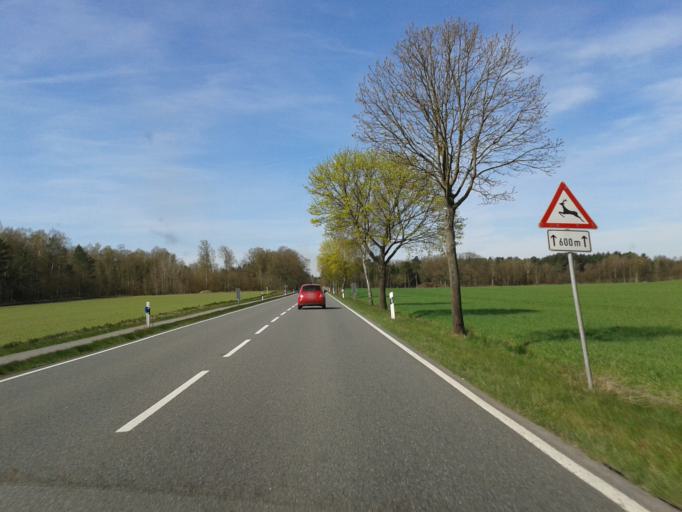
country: DE
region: Lower Saxony
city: Fassberg
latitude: 52.9551
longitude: 10.1425
